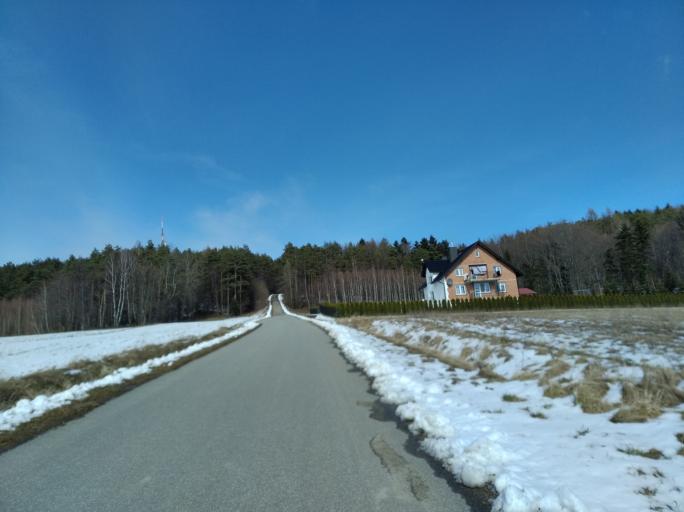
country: PL
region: Subcarpathian Voivodeship
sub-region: Powiat krosnienski
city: Korczyna
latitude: 49.7495
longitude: 21.8146
